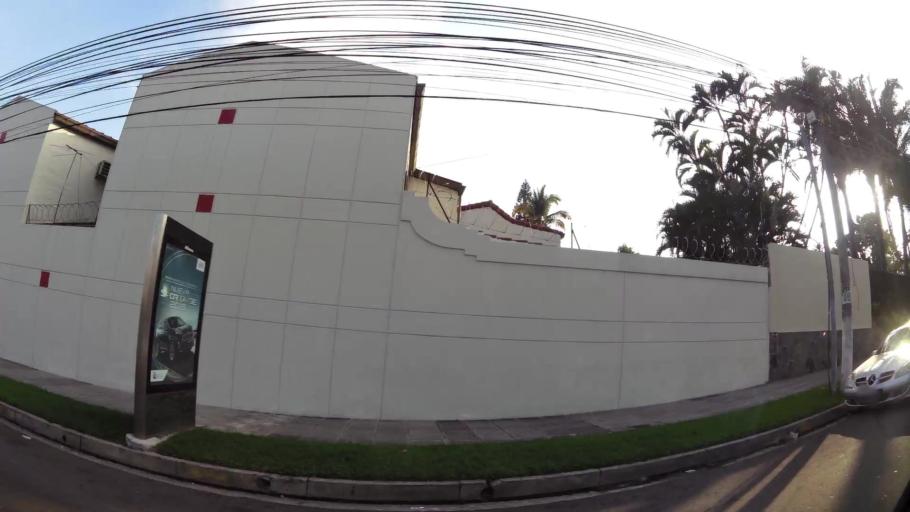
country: SV
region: La Libertad
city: Antiguo Cuscatlan
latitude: 13.6955
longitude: -89.2311
